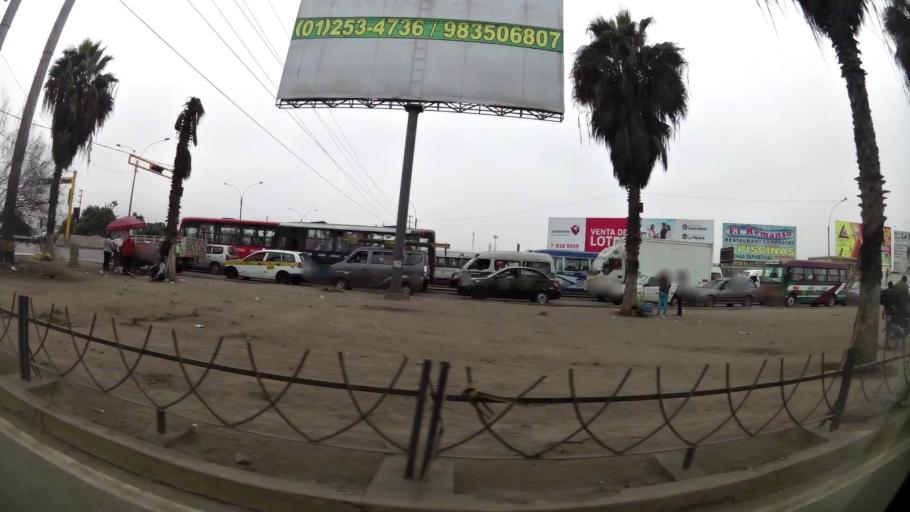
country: PE
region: Lima
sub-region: Lima
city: Independencia
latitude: -11.9307
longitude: -77.0722
